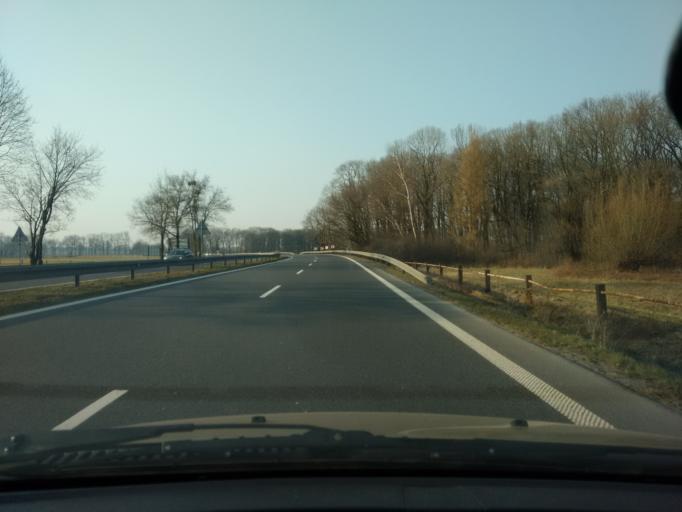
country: PL
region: Silesian Voivodeship
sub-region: Powiat cieszynski
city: Drogomysl
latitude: 49.8566
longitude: 18.7589
